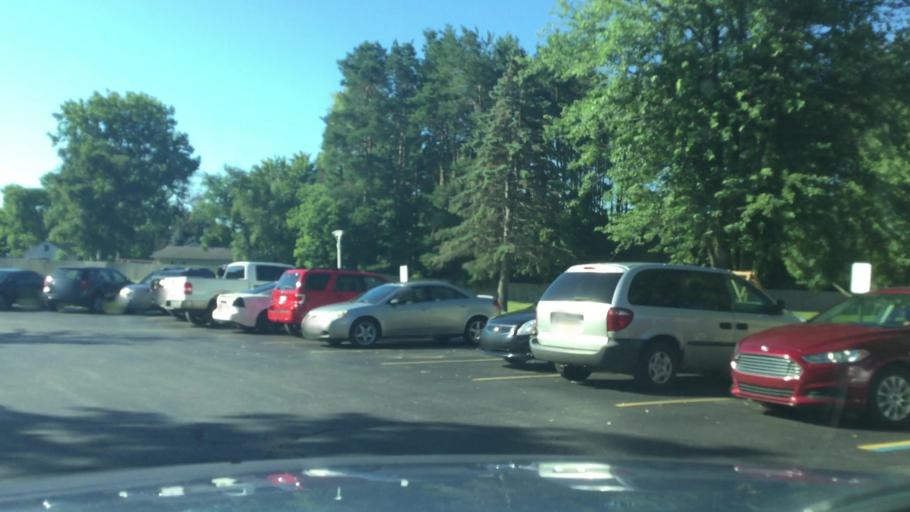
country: US
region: Michigan
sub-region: Saginaw County
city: Shields
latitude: 43.4220
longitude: -84.0537
